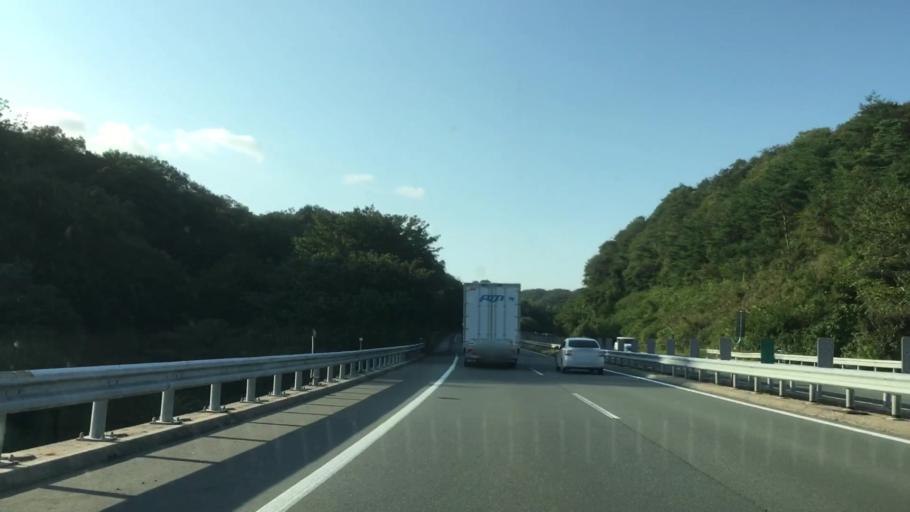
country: JP
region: Yamaguchi
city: Ogori-shimogo
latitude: 34.1608
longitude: 131.3296
